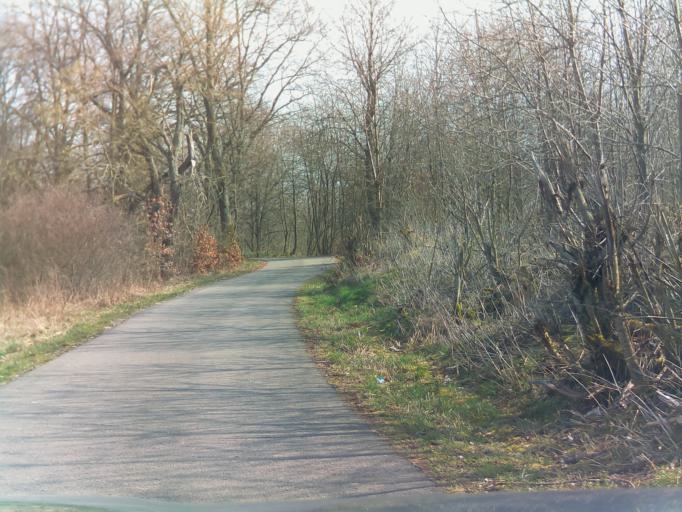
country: DE
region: Rheinland-Pfalz
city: Mettweiler
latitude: 49.5937
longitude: 7.3146
